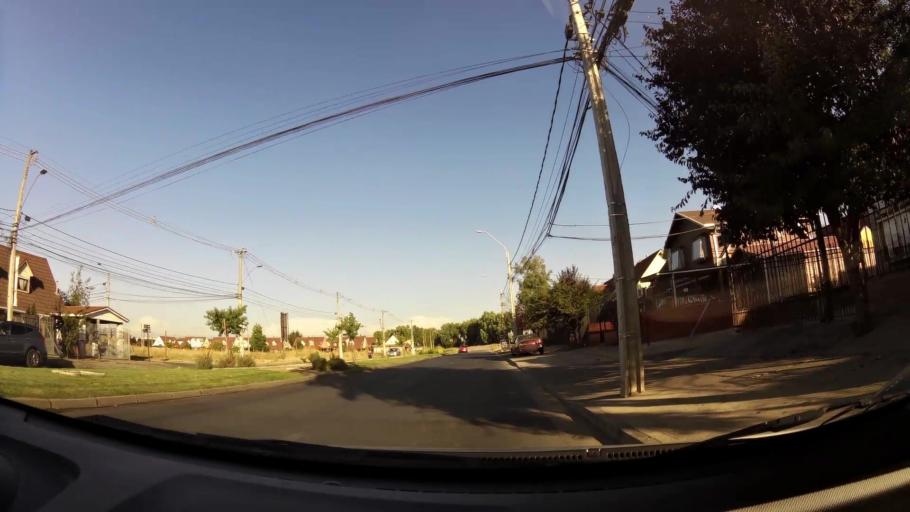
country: CL
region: Maule
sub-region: Provincia de Talca
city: Talca
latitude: -35.4511
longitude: -71.6731
